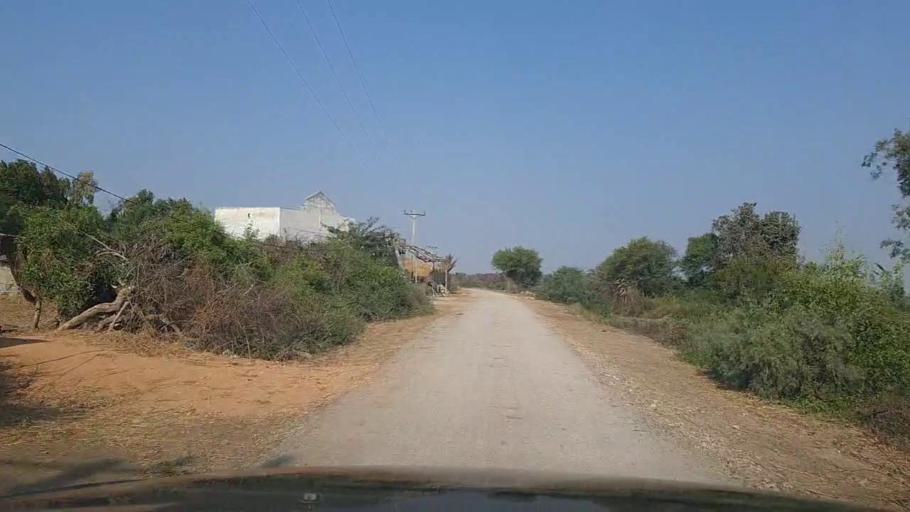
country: PK
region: Sindh
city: Thatta
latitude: 24.6154
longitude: 67.8193
